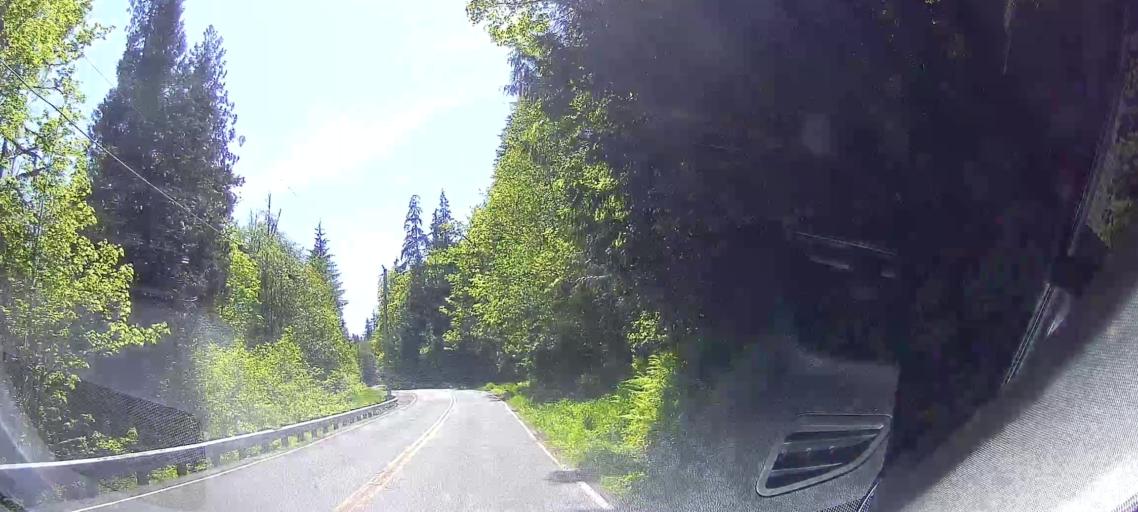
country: US
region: Washington
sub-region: Snohomish County
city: Darrington
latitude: 48.4753
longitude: -121.6455
